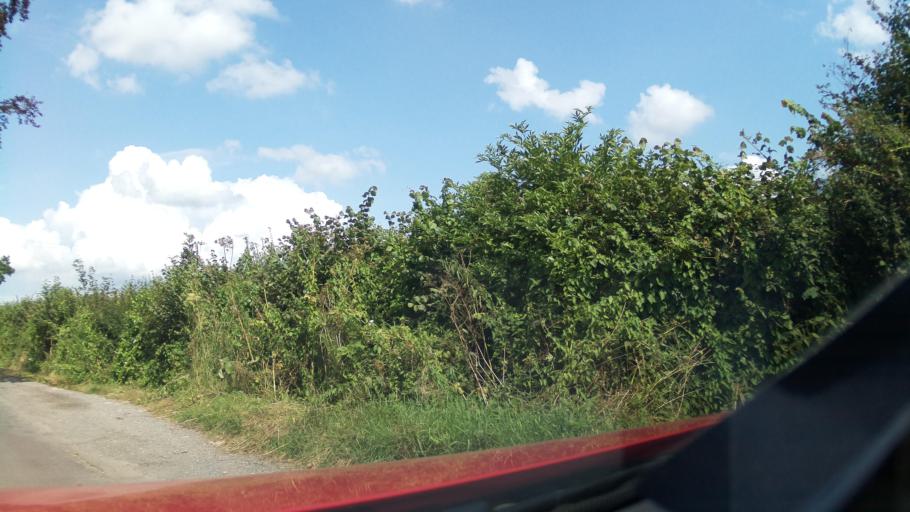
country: GB
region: England
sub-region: Wiltshire
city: Malmesbury
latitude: 51.5592
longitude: -2.1125
